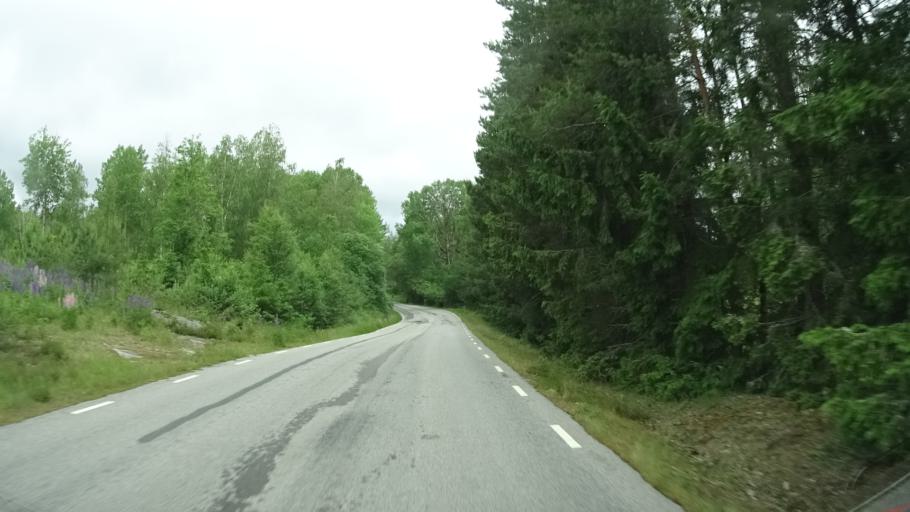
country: SE
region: Joenkoeping
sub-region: Eksjo Kommun
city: Mariannelund
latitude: 57.6991
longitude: 15.6578
